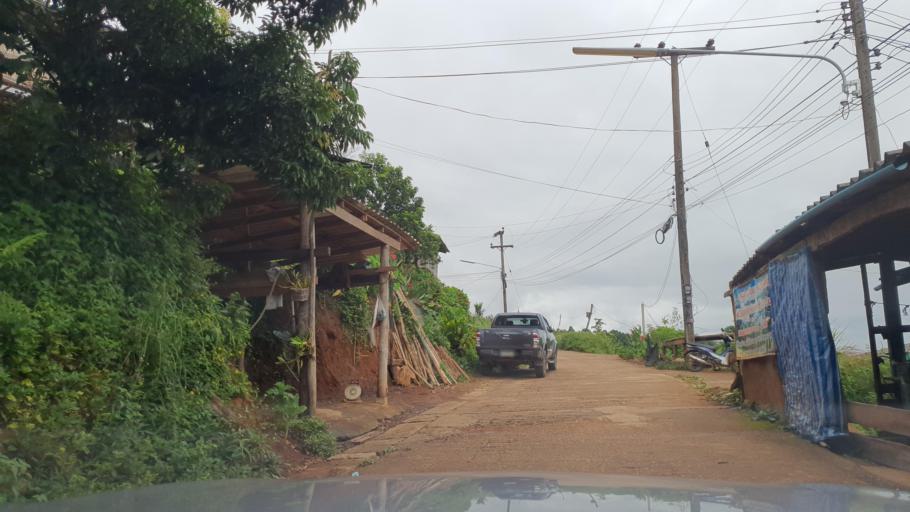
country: TH
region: Chiang Mai
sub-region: Amphoe Chiang Dao
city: Chiang Dao
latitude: 19.2602
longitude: 98.9216
